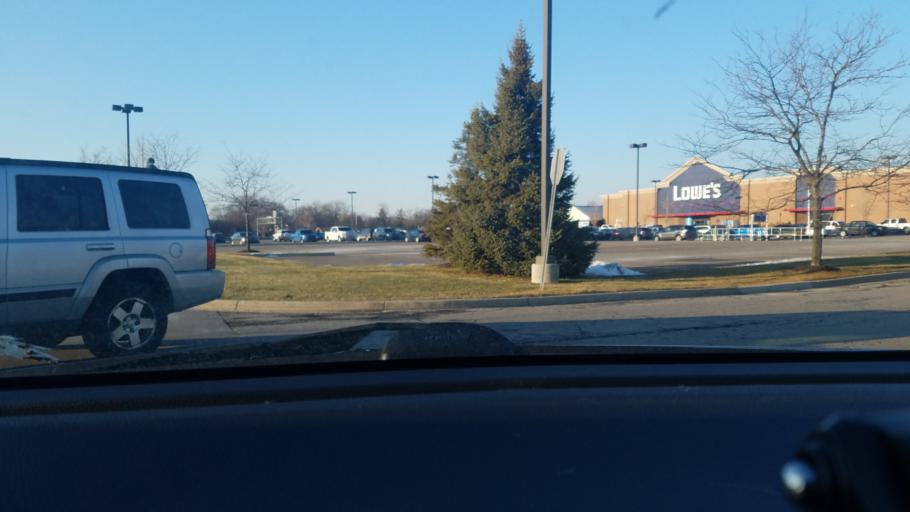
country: US
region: Michigan
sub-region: Wayne County
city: Allen Park
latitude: 42.2788
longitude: -83.2132
